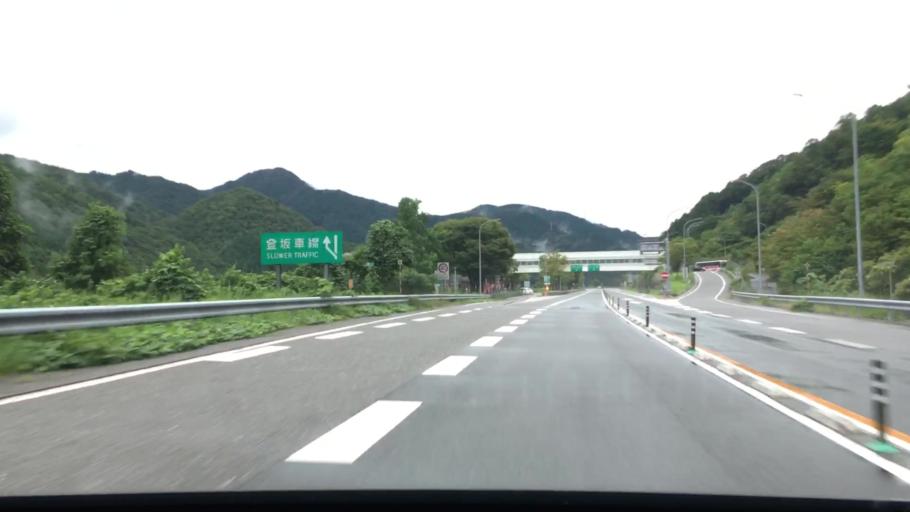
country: JP
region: Hyogo
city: Nishiwaki
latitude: 35.2151
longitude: 134.7936
